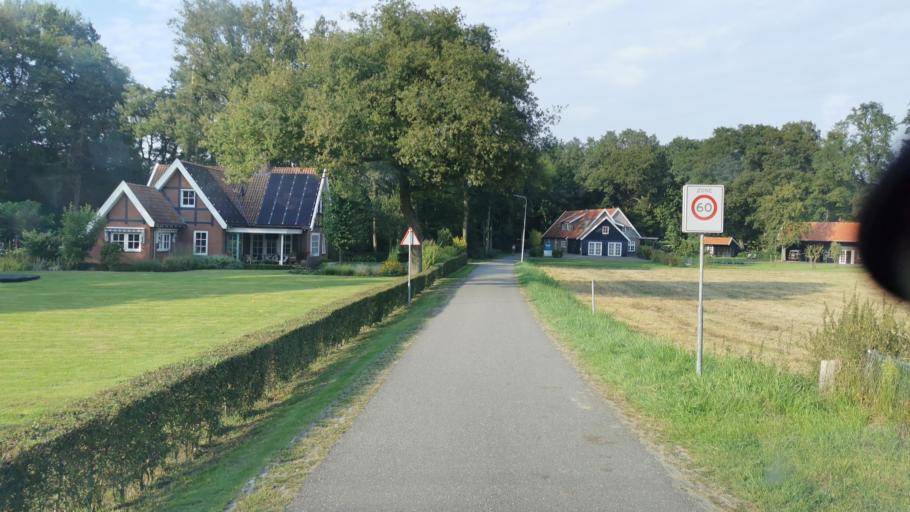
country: NL
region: Overijssel
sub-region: Gemeente Oldenzaal
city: Oldenzaal
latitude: 52.3069
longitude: 6.9495
